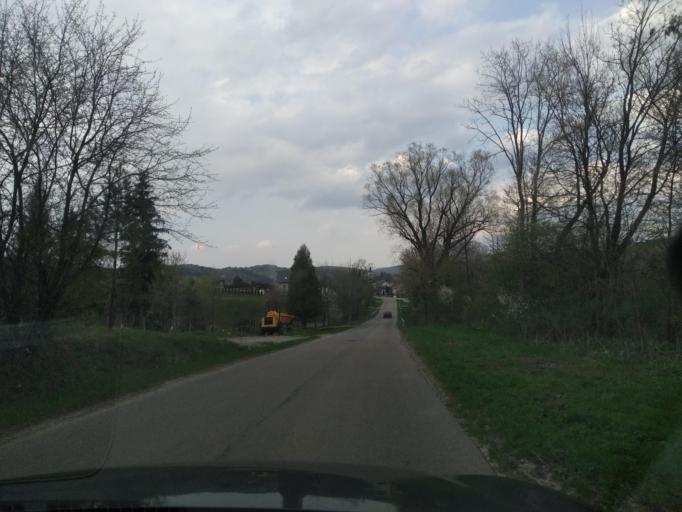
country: PL
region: Subcarpathian Voivodeship
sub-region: Powiat sanocki
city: Czaszyn
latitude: 49.4165
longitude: 22.2344
